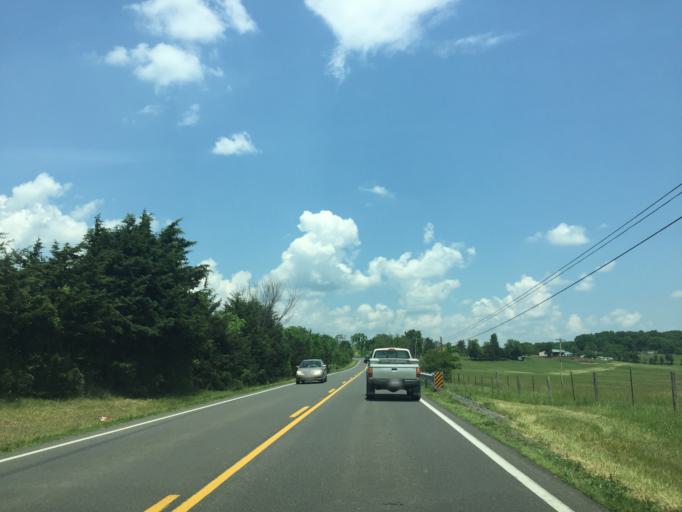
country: US
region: Virginia
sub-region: Shenandoah County
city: Strasburg
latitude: 39.0682
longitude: -78.3709
